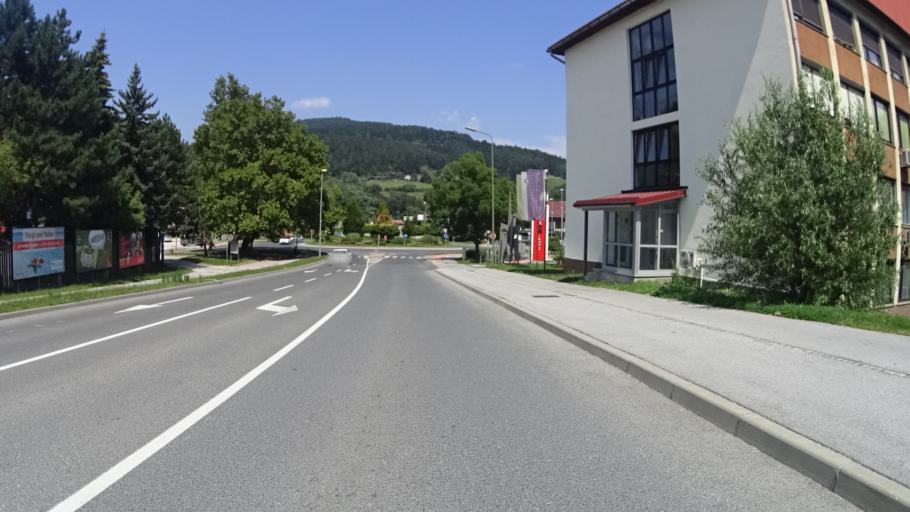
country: SI
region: Ravne na Koroskem
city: Ravne na Koroskem
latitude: 46.5439
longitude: 14.9616
